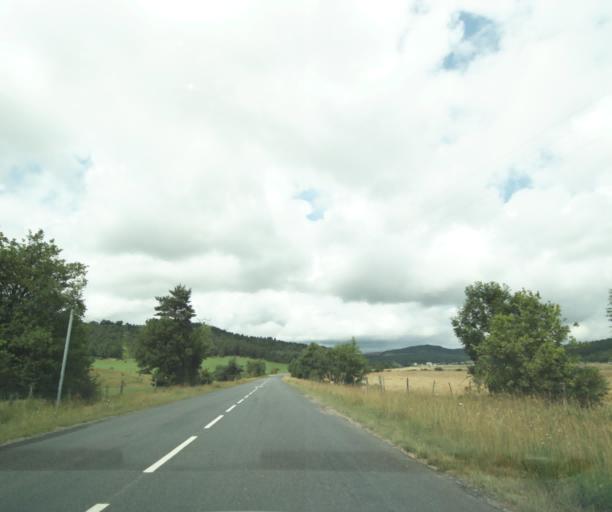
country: FR
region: Midi-Pyrenees
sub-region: Departement de l'Aveyron
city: Severac-le-Chateau
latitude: 44.3706
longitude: 3.1133
